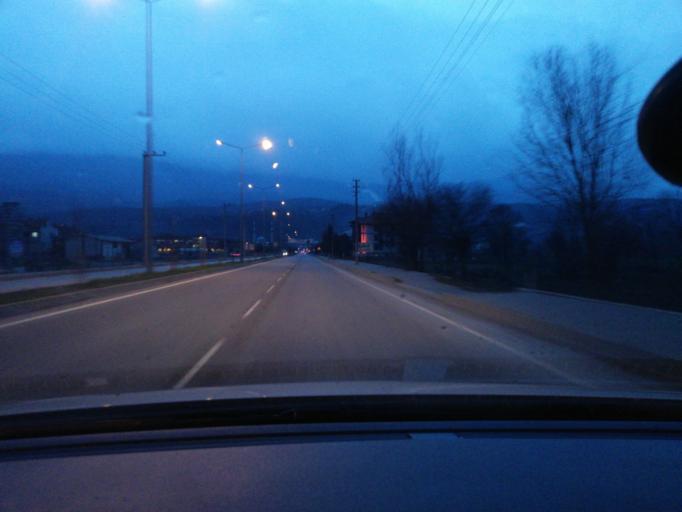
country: TR
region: Bolu
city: Bolu
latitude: 40.6955
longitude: 31.6191
